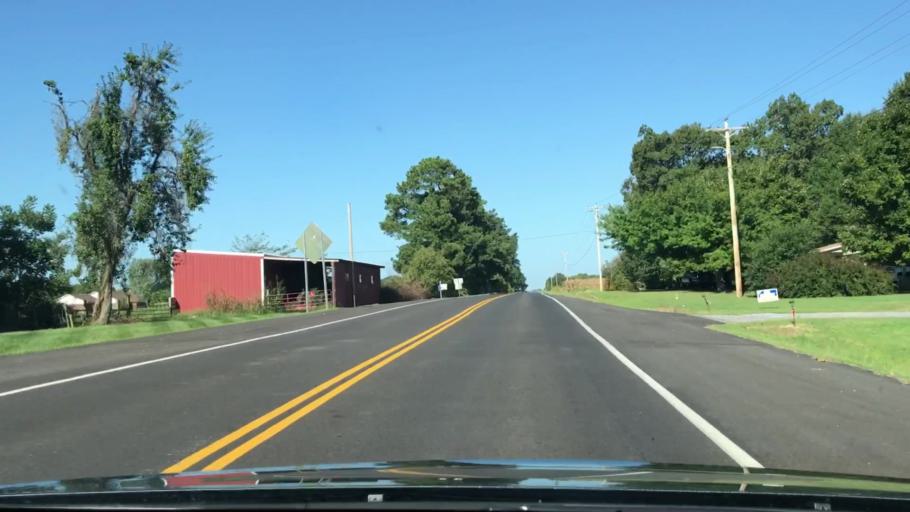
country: US
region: Kentucky
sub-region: Marshall County
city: Benton
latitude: 36.7647
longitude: -88.3151
